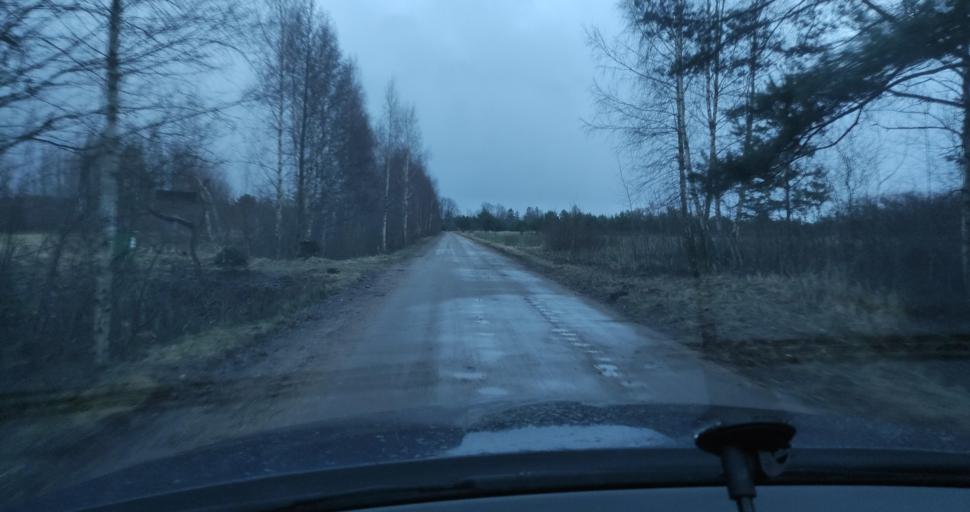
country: LV
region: Pavilostas
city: Pavilosta
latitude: 56.7374
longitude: 21.0688
